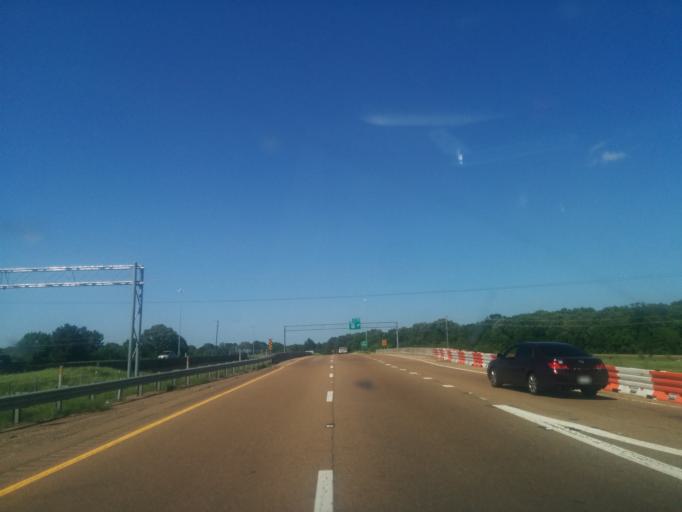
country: US
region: Mississippi
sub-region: Hinds County
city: Jackson
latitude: 32.2996
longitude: -90.2468
